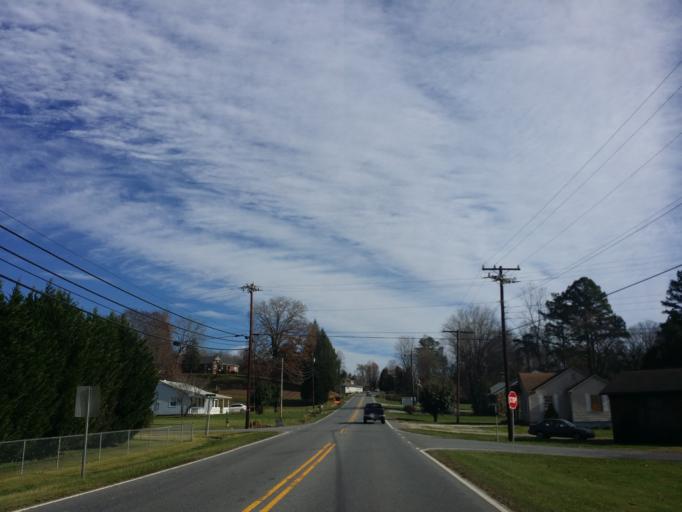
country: US
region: North Carolina
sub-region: McDowell County
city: West Marion
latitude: 35.6861
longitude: -82.0814
